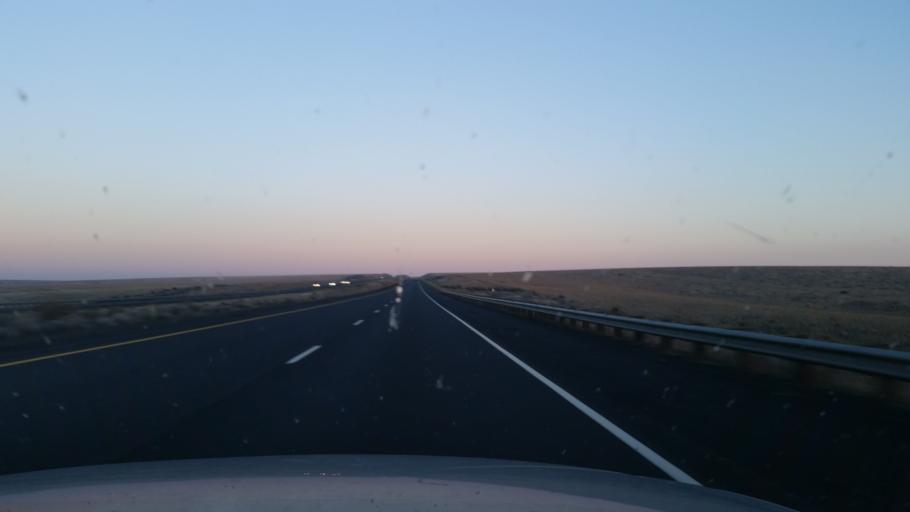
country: US
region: Washington
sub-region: Grant County
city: Warden
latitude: 47.0861
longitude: -118.7556
